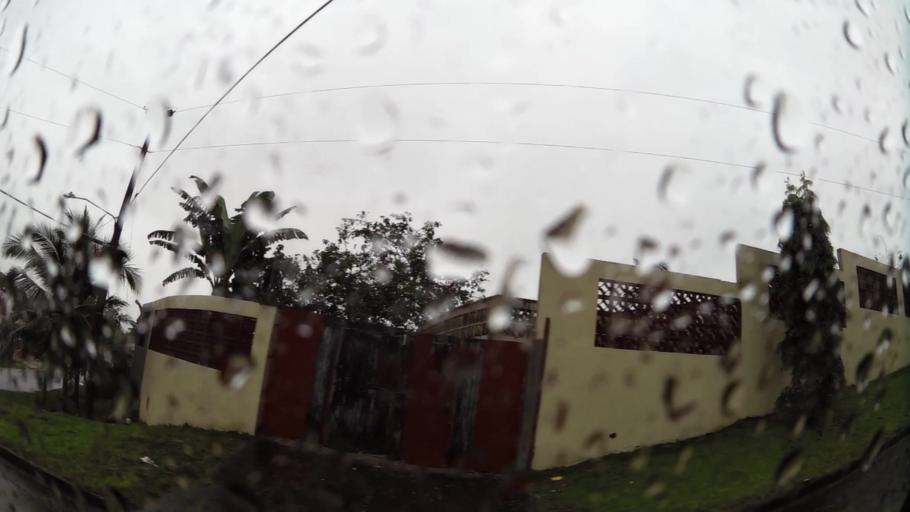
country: PA
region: Colon
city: Sabanitas
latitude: 9.3403
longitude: -79.8084
